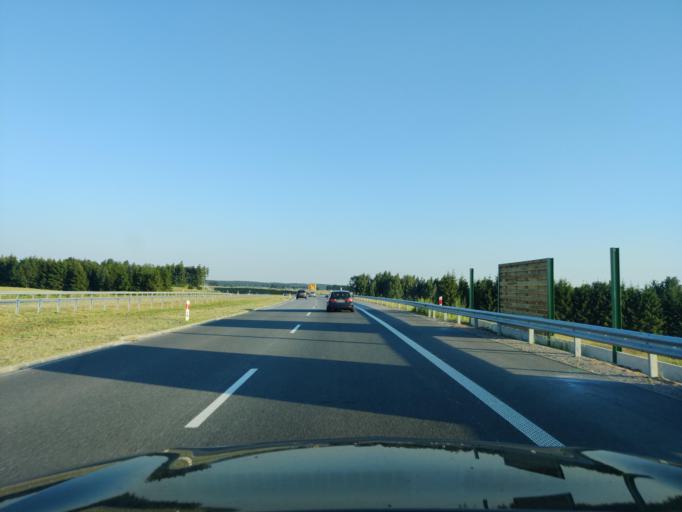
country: PL
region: Masovian Voivodeship
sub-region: Powiat mlawski
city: Wisniewo
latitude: 53.0111
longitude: 20.3368
